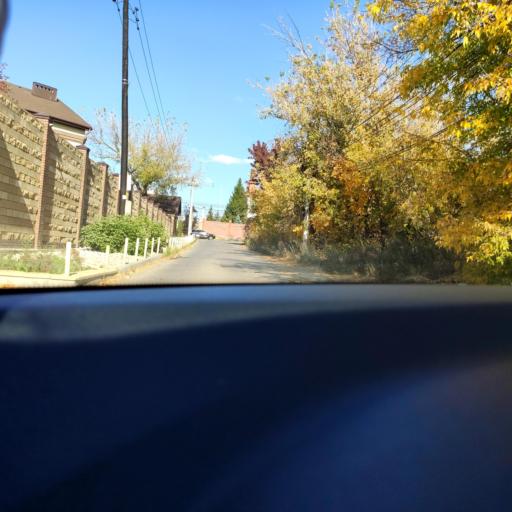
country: RU
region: Samara
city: Samara
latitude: 53.2674
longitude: 50.1936
